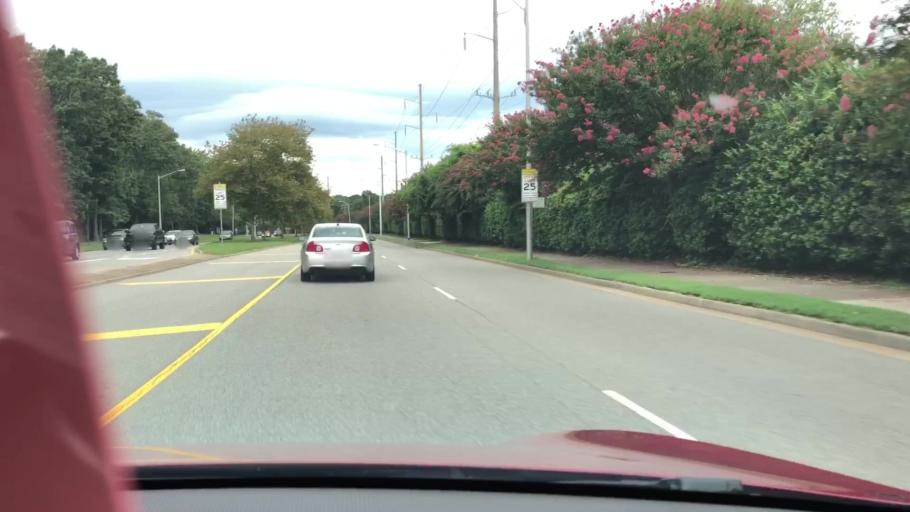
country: US
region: Virginia
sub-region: City of Virginia Beach
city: Virginia Beach
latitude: 36.8865
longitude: -76.0490
